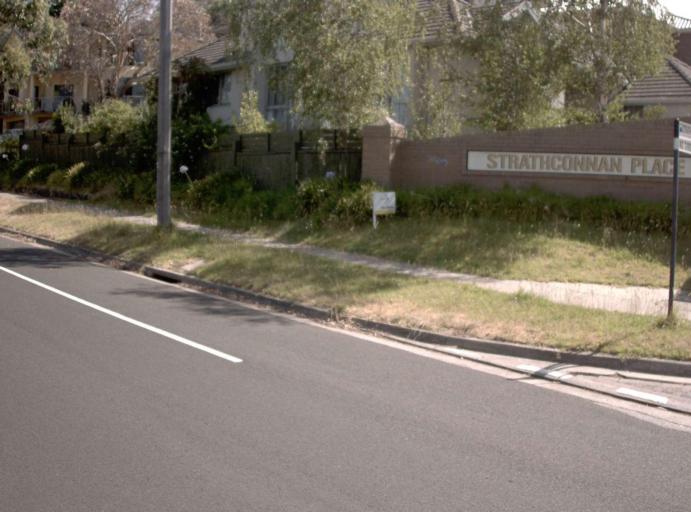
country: AU
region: Victoria
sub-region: Monash
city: Mulgrave
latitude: -37.9036
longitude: 145.1897
